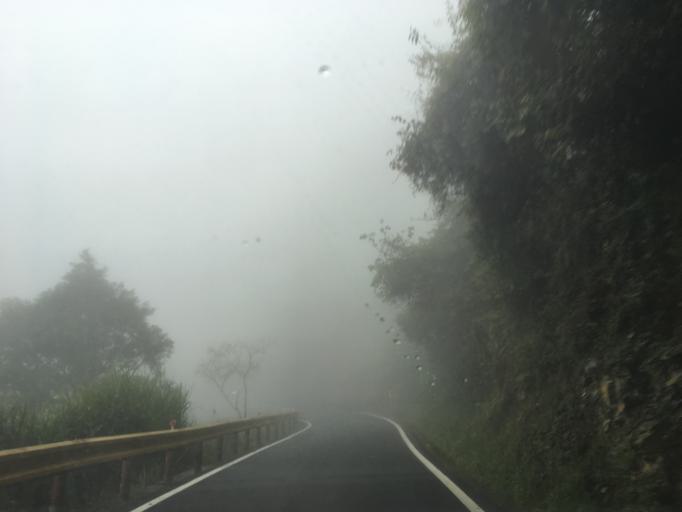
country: TW
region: Taiwan
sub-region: Hualien
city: Hualian
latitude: 24.1957
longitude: 121.4245
